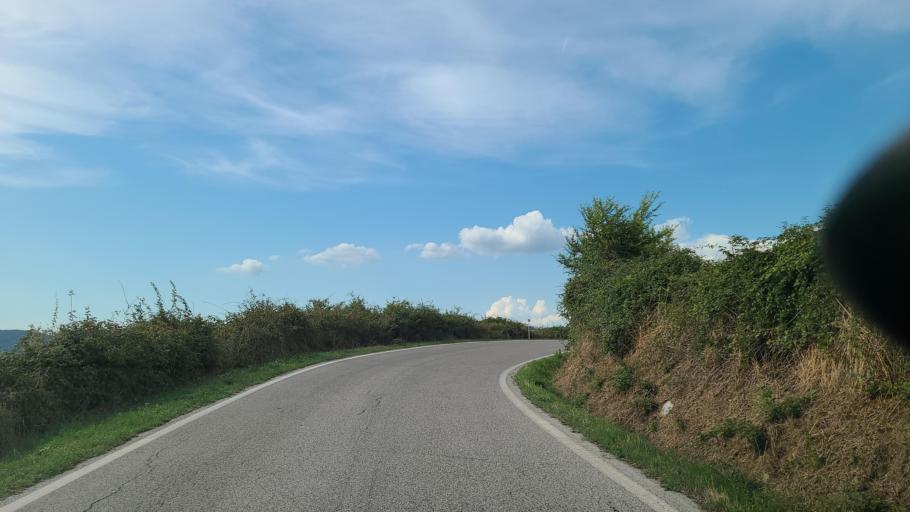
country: IT
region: Tuscany
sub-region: Provincia di Siena
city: San Gimignano
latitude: 43.4050
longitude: 10.9745
